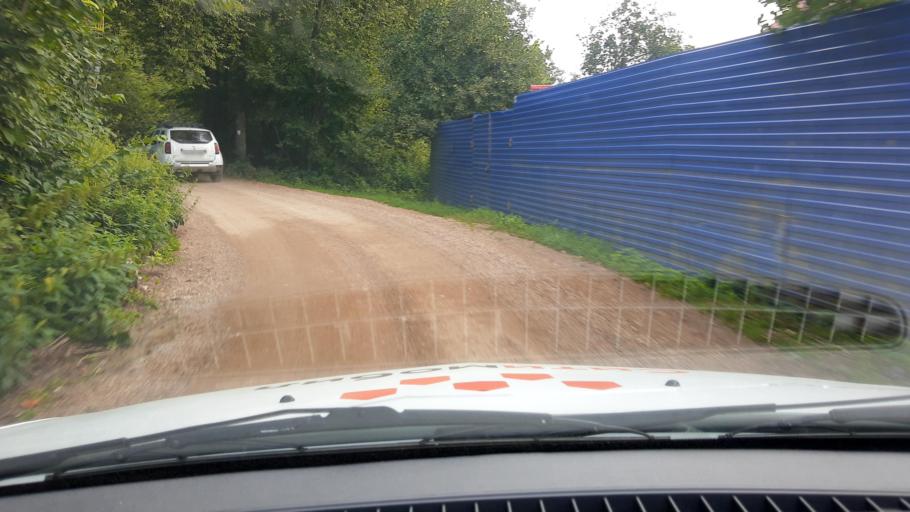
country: RU
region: Bashkortostan
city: Kabakovo
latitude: 54.7077
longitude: 56.1380
